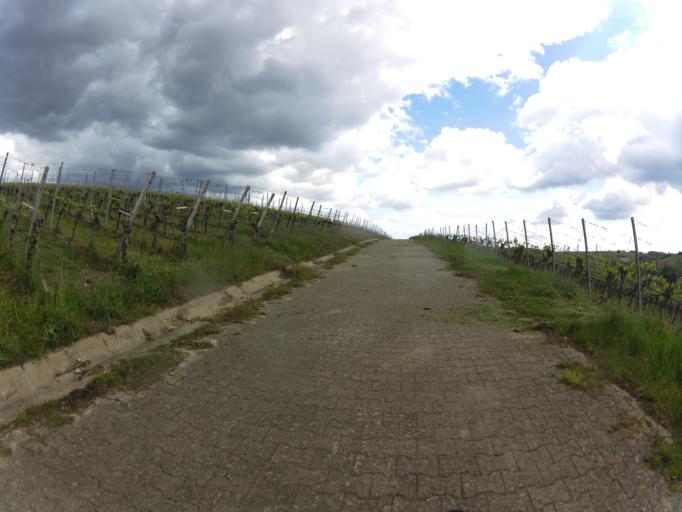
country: DE
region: Bavaria
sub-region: Regierungsbezirk Unterfranken
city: Nordheim
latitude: 49.8404
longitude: 10.1819
